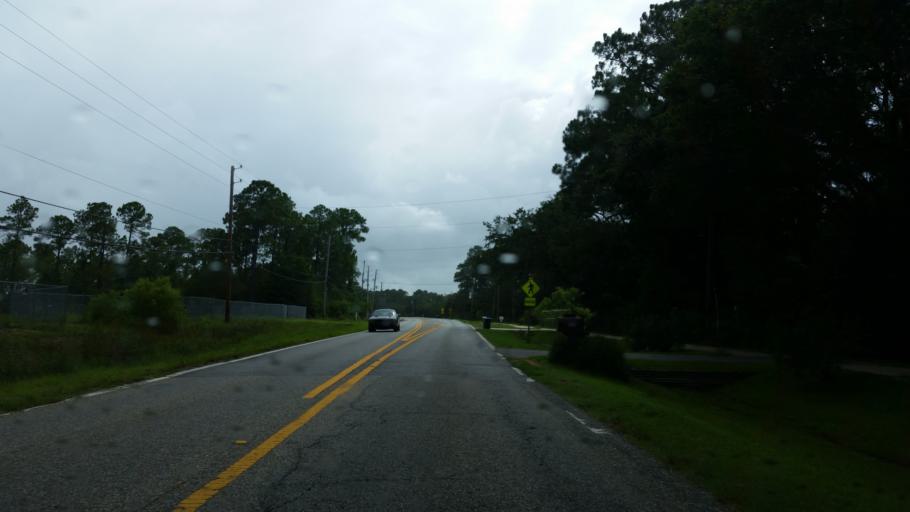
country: US
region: Florida
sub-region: Santa Rosa County
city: Woodlawn Beach
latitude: 30.4103
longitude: -86.9958
